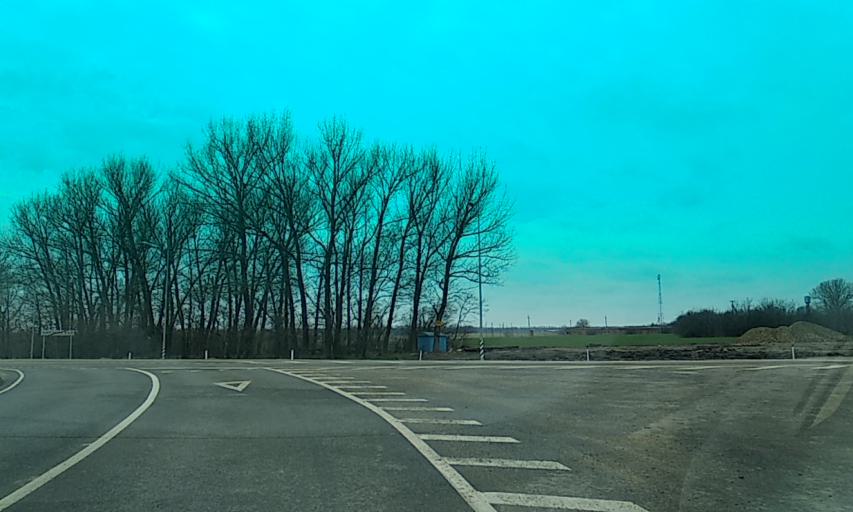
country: RU
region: Krasnodarskiy
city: Ust'-Labinsk
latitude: 45.3671
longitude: 39.6967
